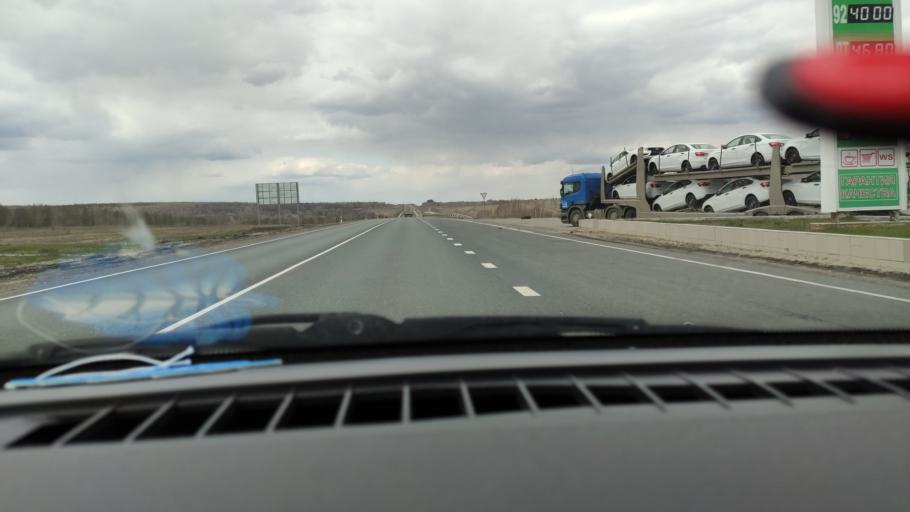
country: RU
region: Saratov
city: Shikhany
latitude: 52.1350
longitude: 47.2204
